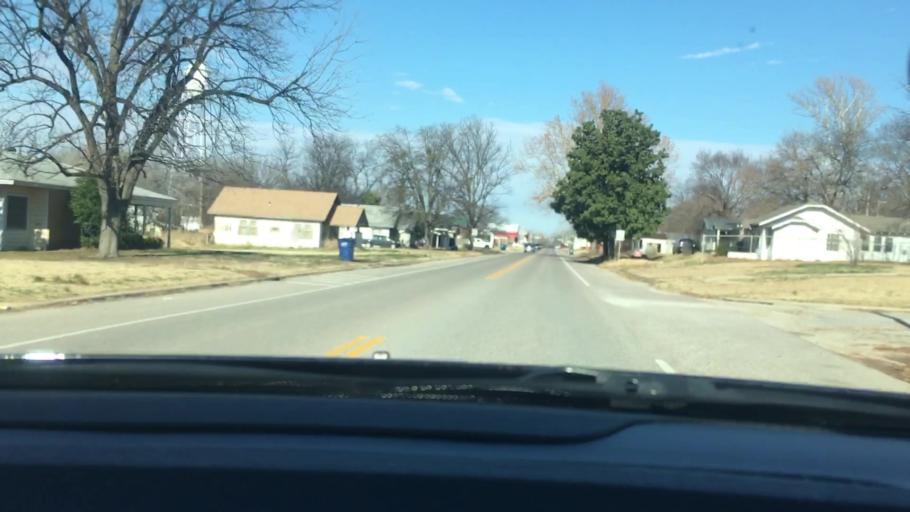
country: US
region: Oklahoma
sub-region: Garvin County
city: Wynnewood
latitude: 34.6376
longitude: -97.1694
